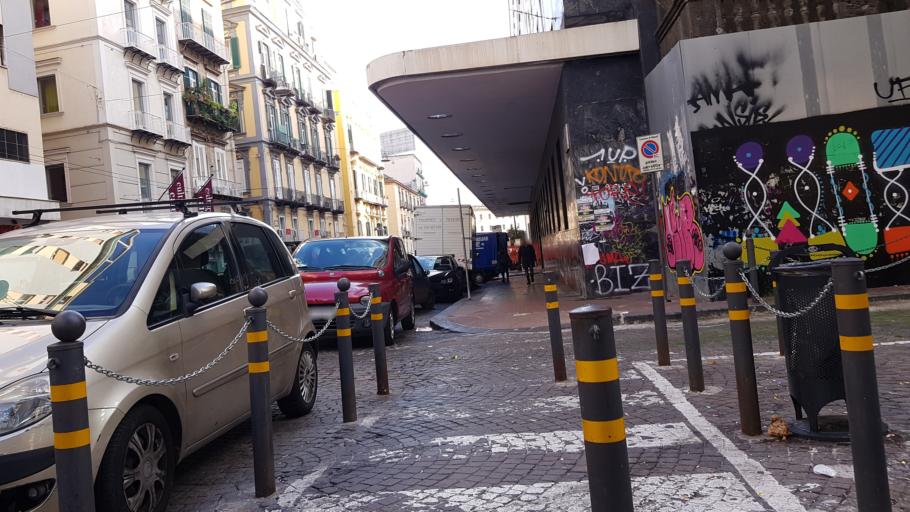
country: IT
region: Campania
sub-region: Provincia di Napoli
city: Napoli
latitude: 40.8444
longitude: 14.2515
